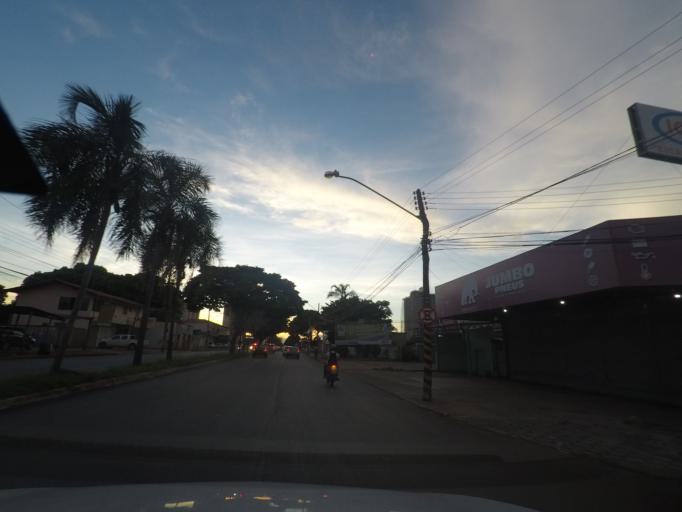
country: BR
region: Goias
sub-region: Goiania
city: Goiania
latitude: -16.6964
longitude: -49.3062
